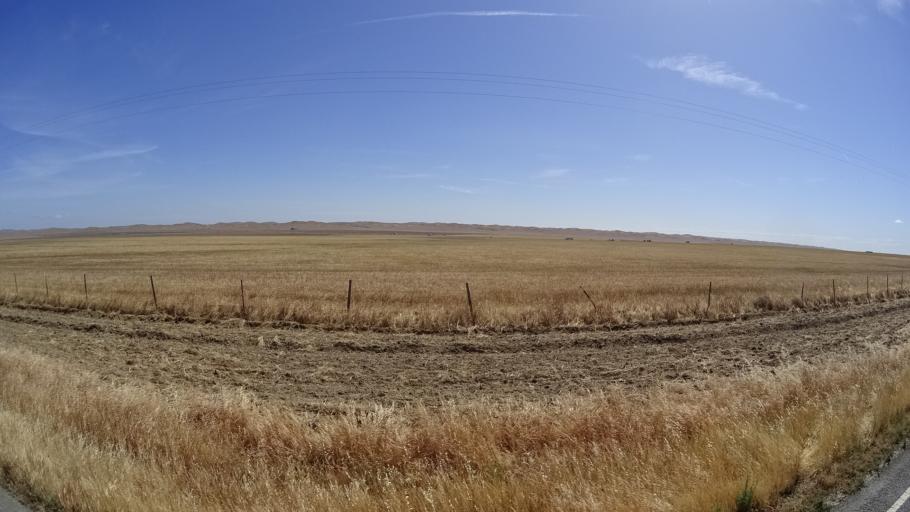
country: US
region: California
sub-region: Kings County
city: Avenal
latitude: 35.8992
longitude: -120.0519
